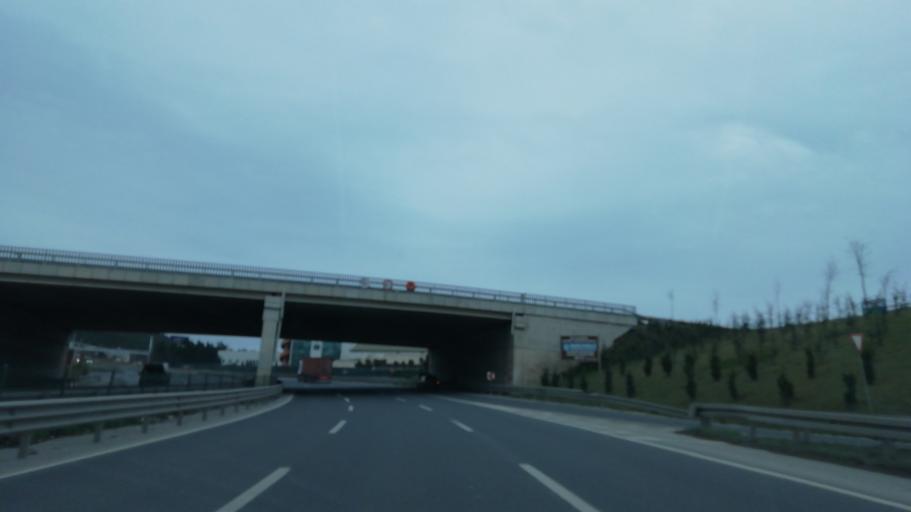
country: TR
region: Kocaeli
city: Tavsancil
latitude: 40.7800
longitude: 29.5407
